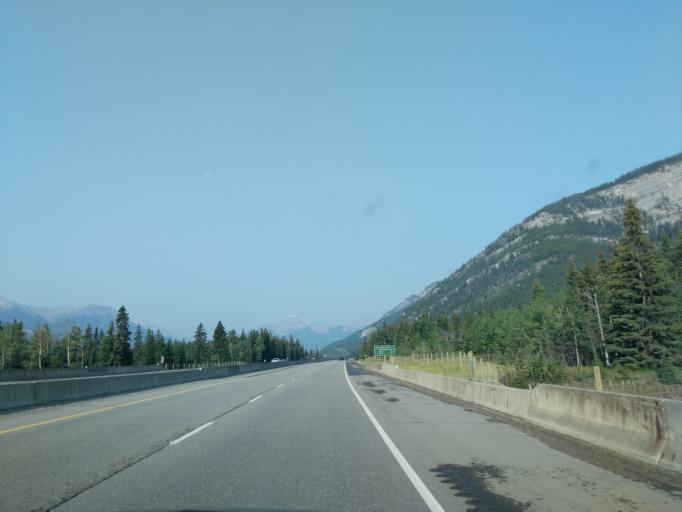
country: CA
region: Alberta
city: Banff
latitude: 51.1957
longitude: -115.5529
